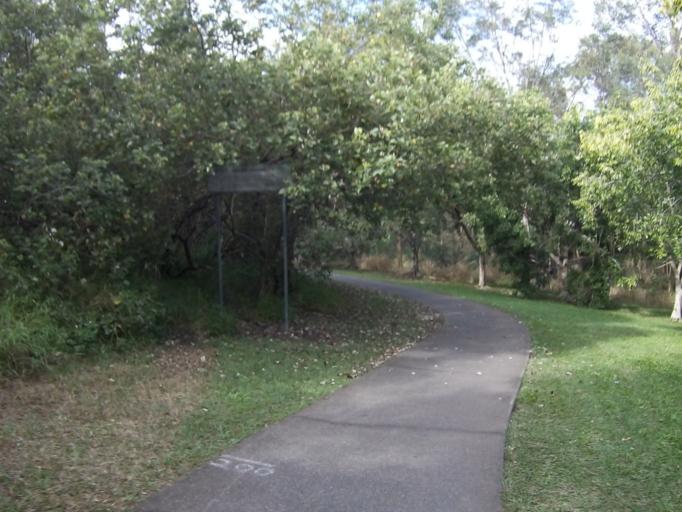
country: AU
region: Queensland
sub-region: Brisbane
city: Annerley
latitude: -27.5138
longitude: 153.0414
